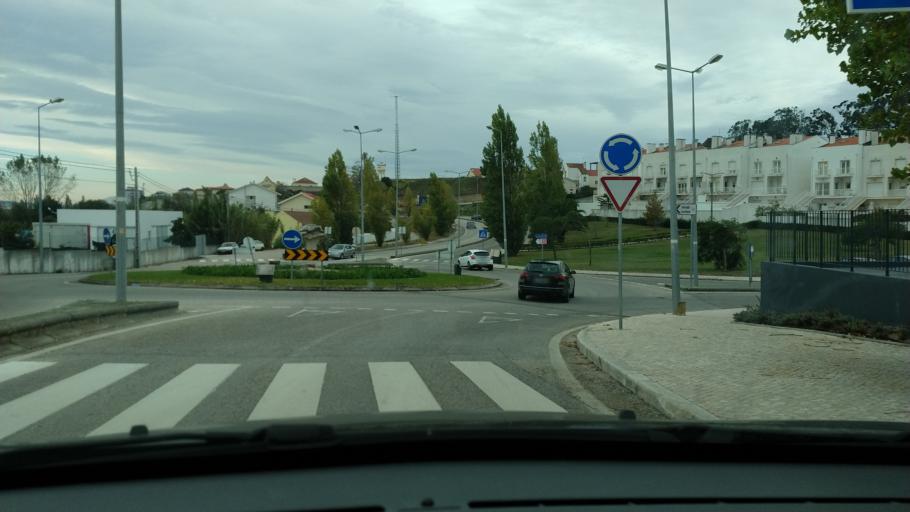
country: PT
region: Coimbra
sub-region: Figueira da Foz
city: Figueira da Foz
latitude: 40.1572
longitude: -8.8495
